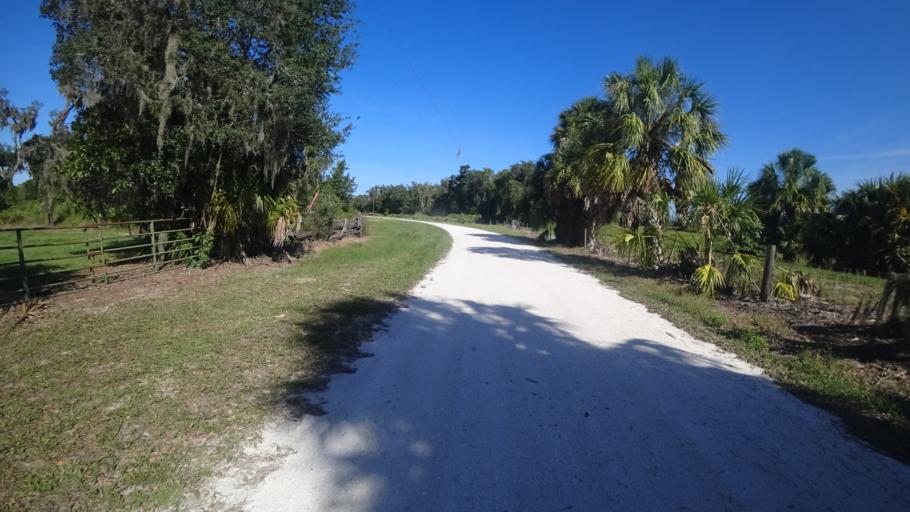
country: US
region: Florida
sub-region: Hillsborough County
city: Wimauma
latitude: 27.5931
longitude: -82.1863
